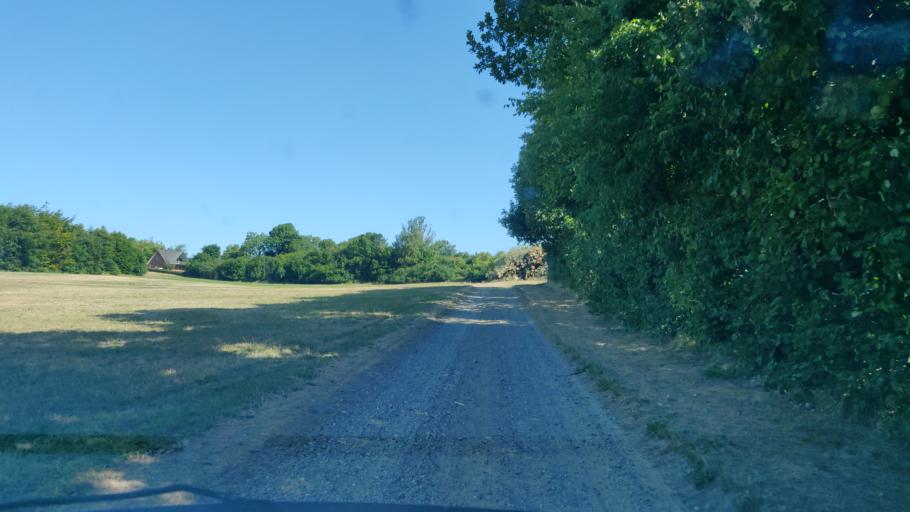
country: DK
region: South Denmark
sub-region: Fredericia Kommune
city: Taulov
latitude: 55.5186
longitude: 9.5635
